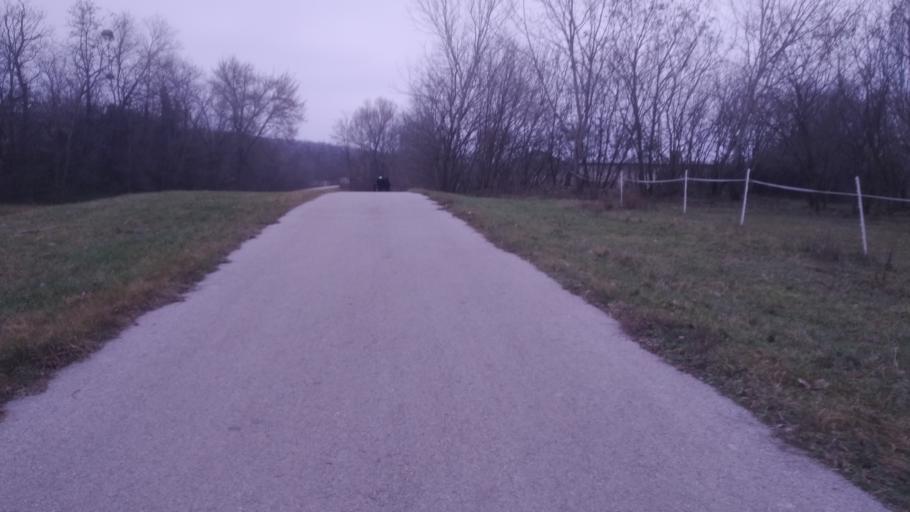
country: HU
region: Komarom-Esztergom
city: Dunaalmas
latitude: 47.7238
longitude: 18.3134
